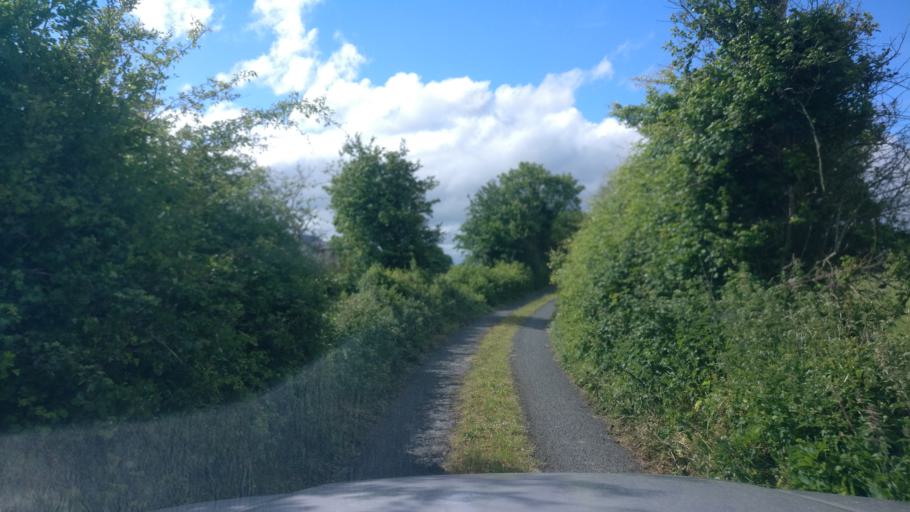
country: IE
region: Connaught
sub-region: County Galway
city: Loughrea
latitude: 53.2347
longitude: -8.6005
